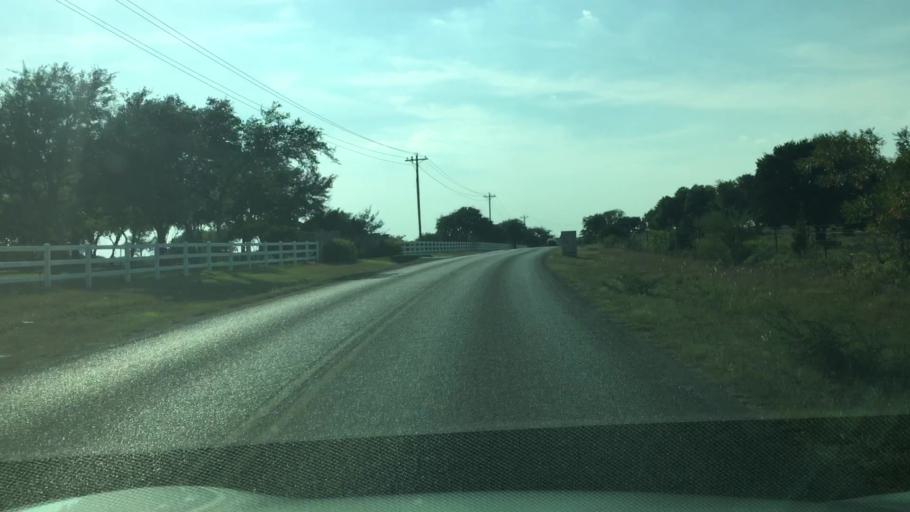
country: US
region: Texas
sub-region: Hays County
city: Dripping Springs
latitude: 30.1488
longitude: -97.9905
